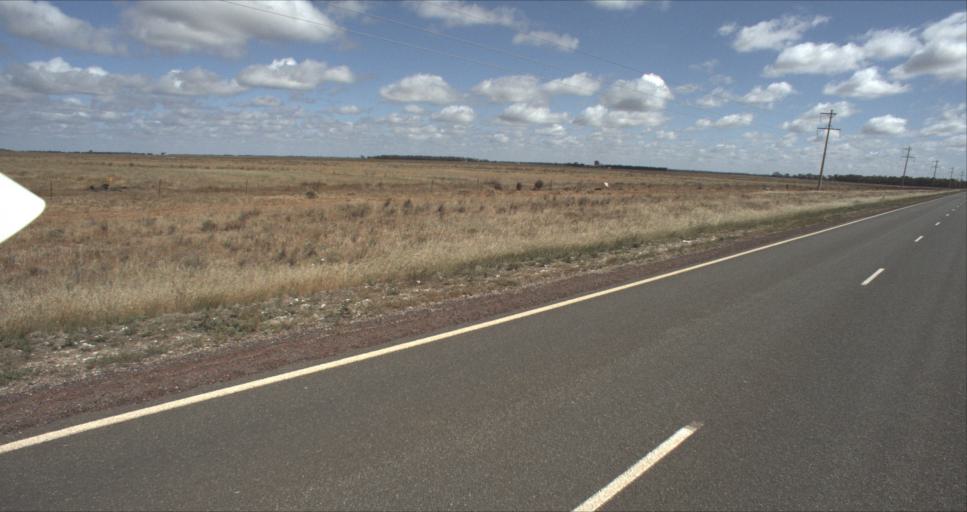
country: AU
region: New South Wales
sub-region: Murrumbidgee Shire
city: Darlington Point
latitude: -34.5869
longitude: 146.1641
